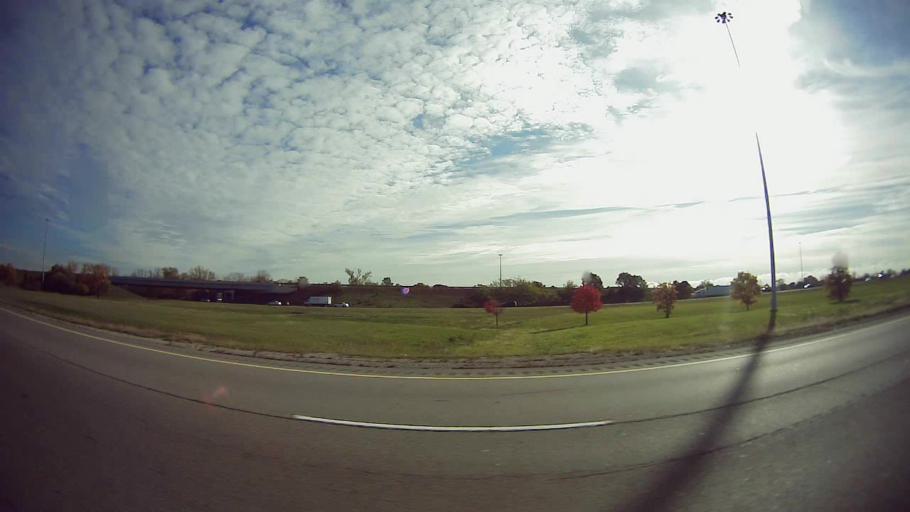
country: US
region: Michigan
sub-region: Wayne County
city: Plymouth
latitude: 42.3900
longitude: -83.4362
